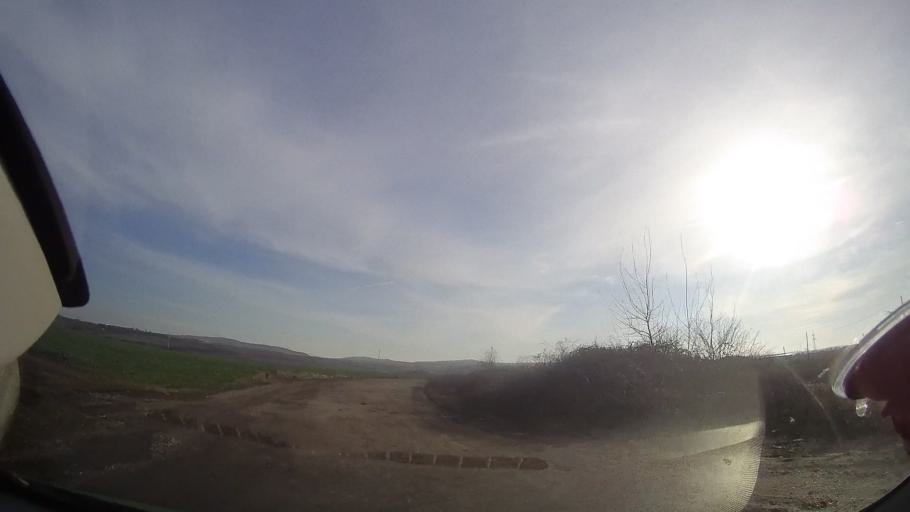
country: RO
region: Bihor
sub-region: Comuna Ciuhoiu
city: Ciuhoiu
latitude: 47.2192
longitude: 22.1342
